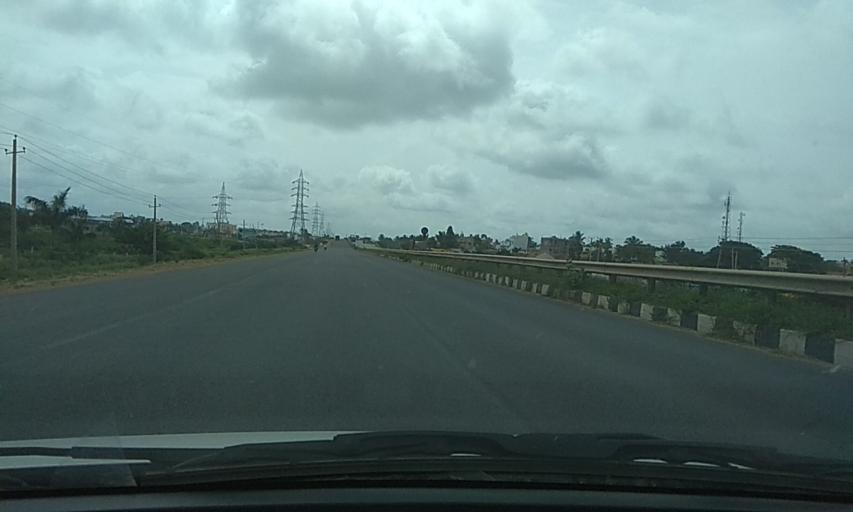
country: IN
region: Karnataka
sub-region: Davanagere
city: Harihar
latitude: 14.4437
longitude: 75.8939
